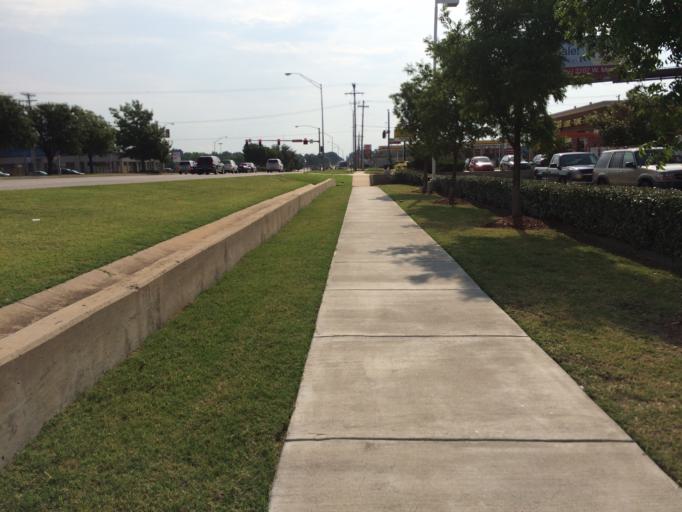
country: US
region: Oklahoma
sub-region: Cleveland County
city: Norman
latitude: 35.2182
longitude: -97.4779
